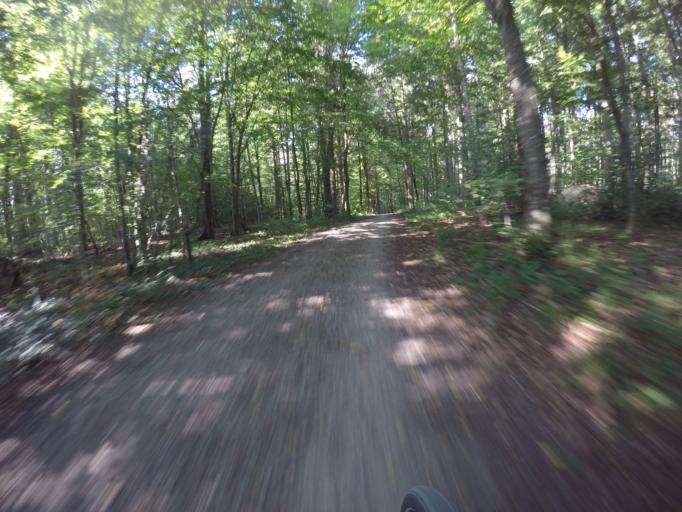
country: DE
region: Baden-Wuerttemberg
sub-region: Regierungsbezirk Stuttgart
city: Altdorf
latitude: 48.6569
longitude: 8.9833
